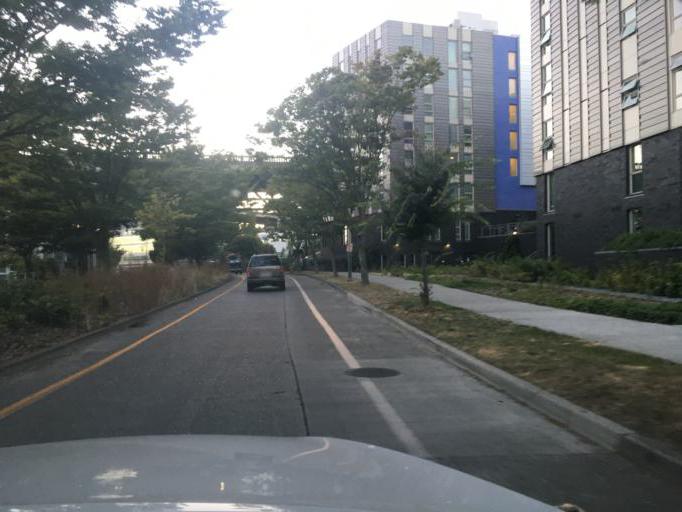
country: US
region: Washington
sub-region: King County
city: Seattle
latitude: 47.6540
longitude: -122.3180
